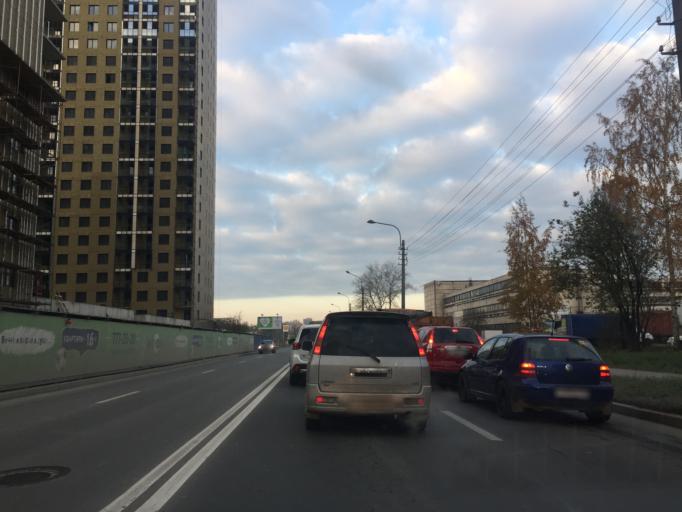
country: RU
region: St.-Petersburg
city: Obukhovo
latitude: 59.8932
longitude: 30.4518
